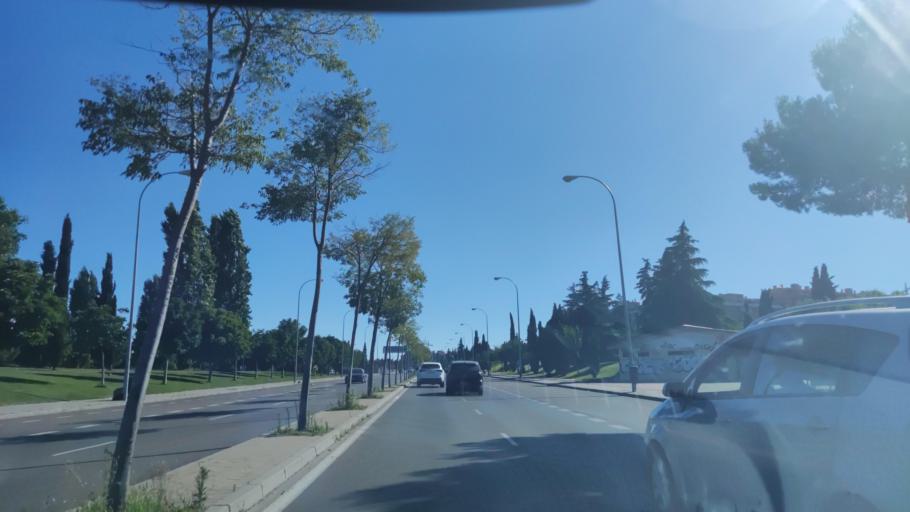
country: ES
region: Madrid
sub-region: Provincia de Madrid
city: Latina
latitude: 40.3723
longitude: -3.7356
